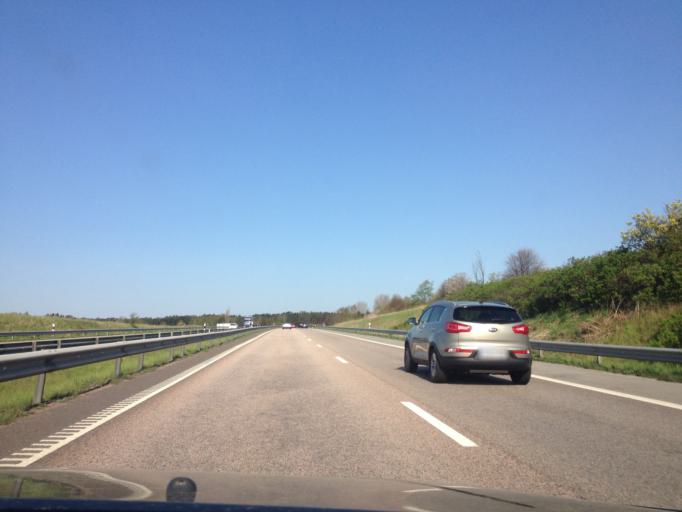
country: SE
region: Skane
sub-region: Kavlinge Kommun
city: Loddekopinge
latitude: 55.7521
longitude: 13.0073
